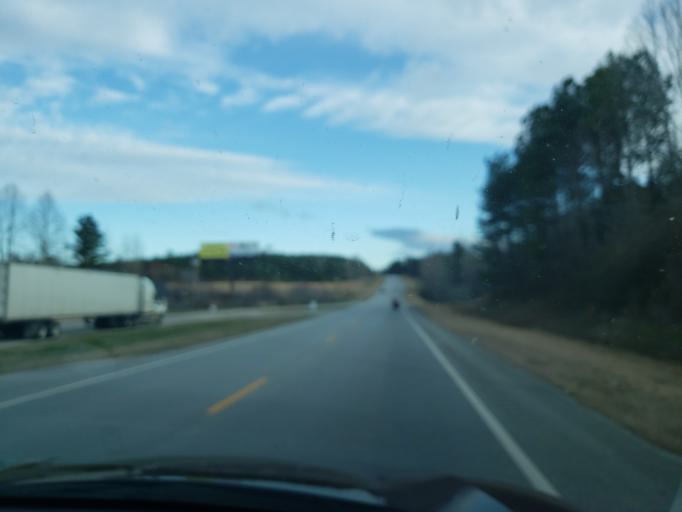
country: US
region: Alabama
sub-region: Randolph County
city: Wedowee
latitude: 33.3408
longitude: -85.4888
